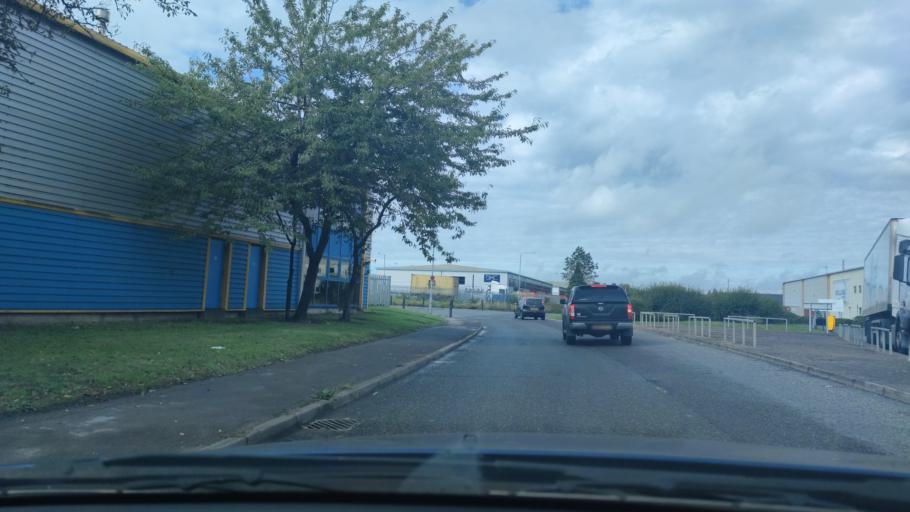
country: GB
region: England
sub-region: Borough of Thurrock
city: Tilbury
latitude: 51.4690
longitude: 0.3445
